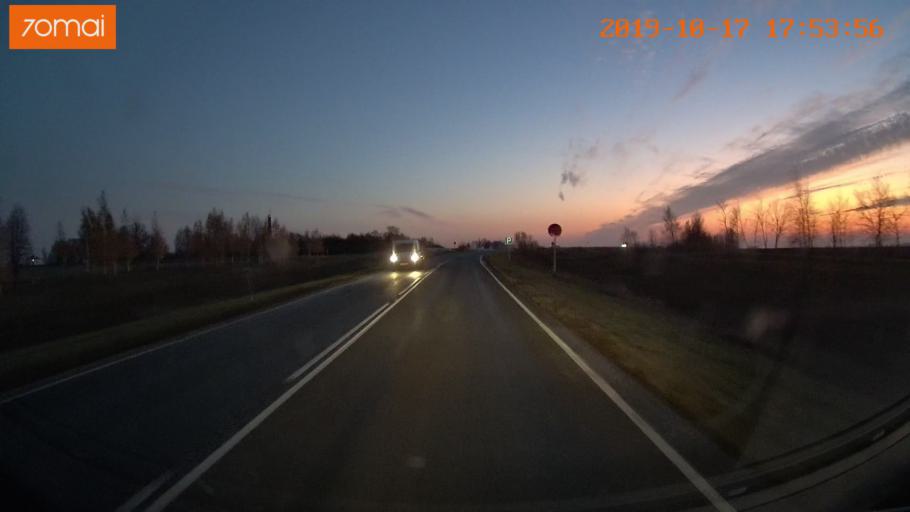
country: RU
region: Tula
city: Kurkino
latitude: 53.6128
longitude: 38.6735
